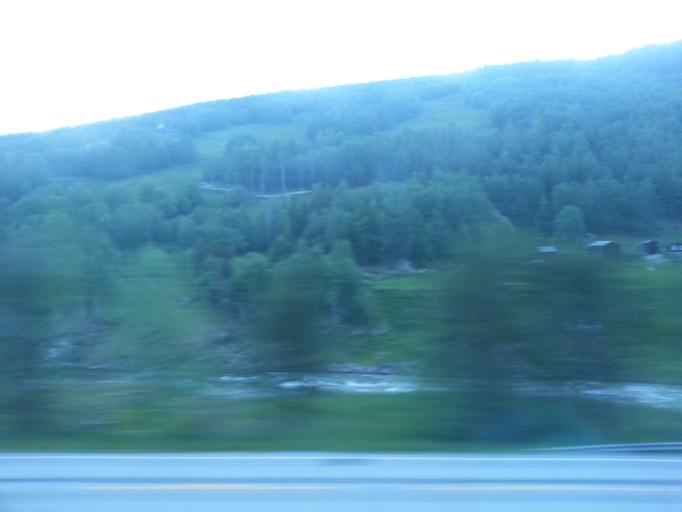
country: NO
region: Oppland
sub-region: Dovre
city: Dovre
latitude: 61.8976
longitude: 9.3879
